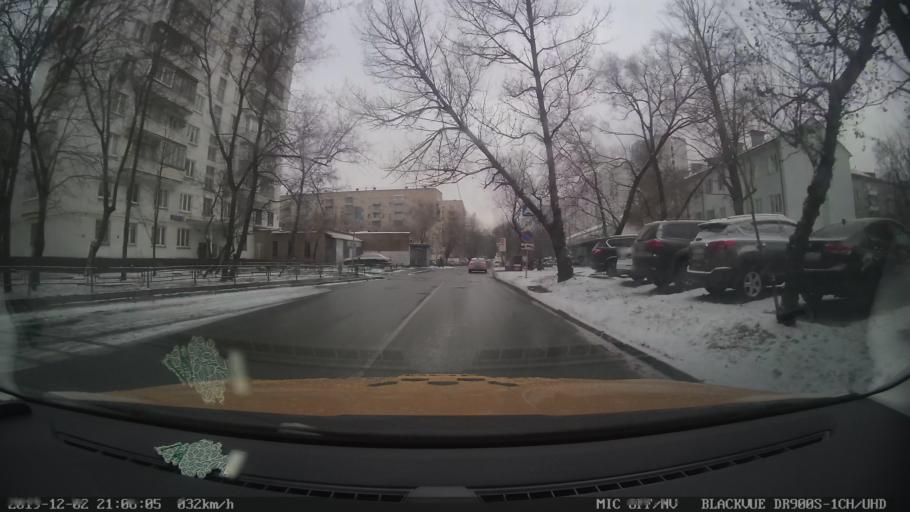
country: RU
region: Moscow
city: Mar'ina Roshcha
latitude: 55.7937
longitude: 37.6243
